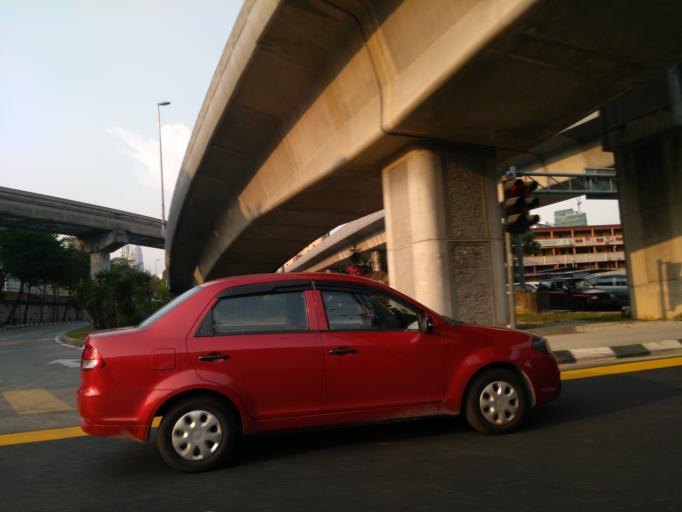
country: MY
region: Kuala Lumpur
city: Kuala Lumpur
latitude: 3.1367
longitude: 101.7037
